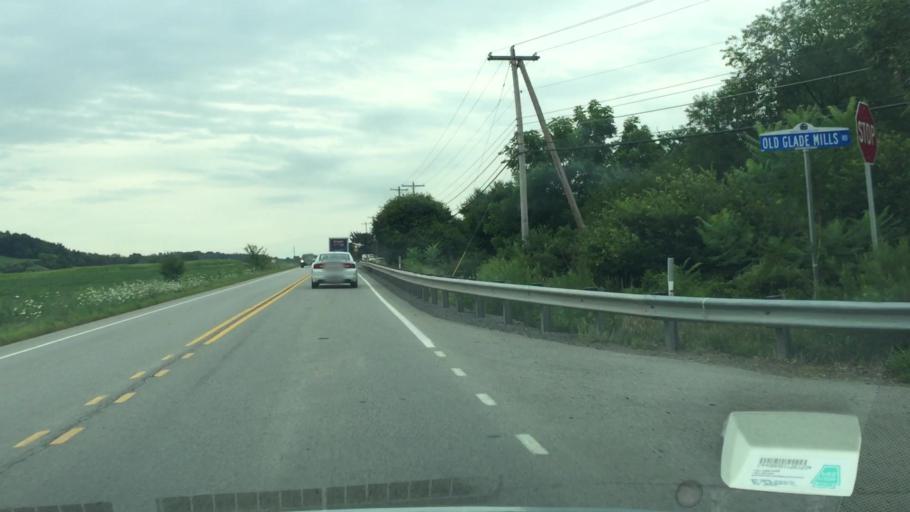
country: US
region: Pennsylvania
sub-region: Butler County
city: Nixon
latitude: 40.7240
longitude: -79.9121
